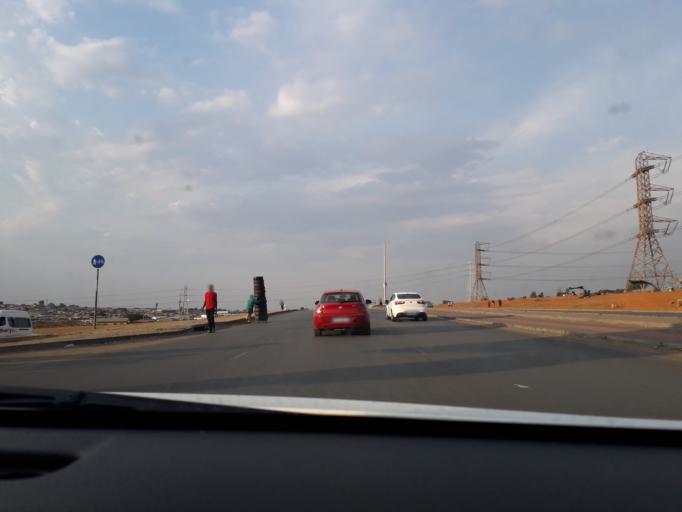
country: ZA
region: Gauteng
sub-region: Ekurhuleni Metropolitan Municipality
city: Tembisa
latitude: -26.0341
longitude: 28.1917
